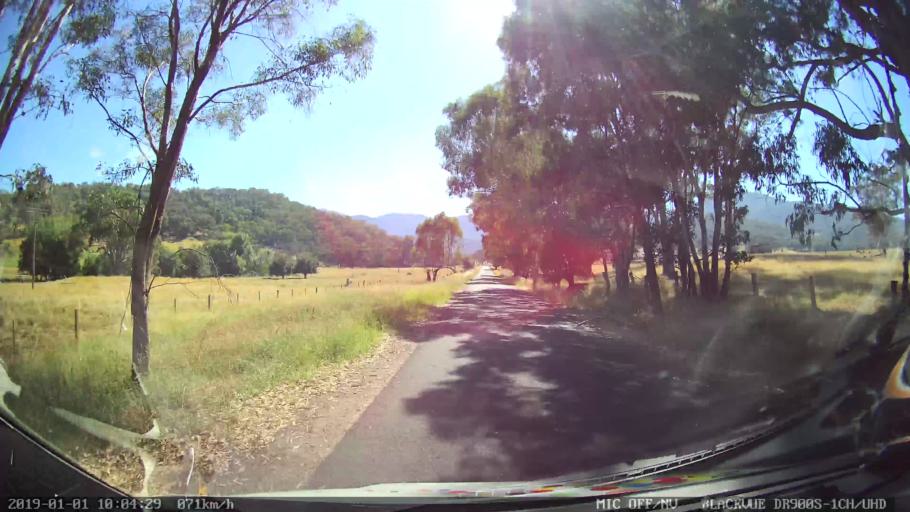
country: AU
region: New South Wales
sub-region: Snowy River
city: Jindabyne
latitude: -36.1757
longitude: 148.1229
